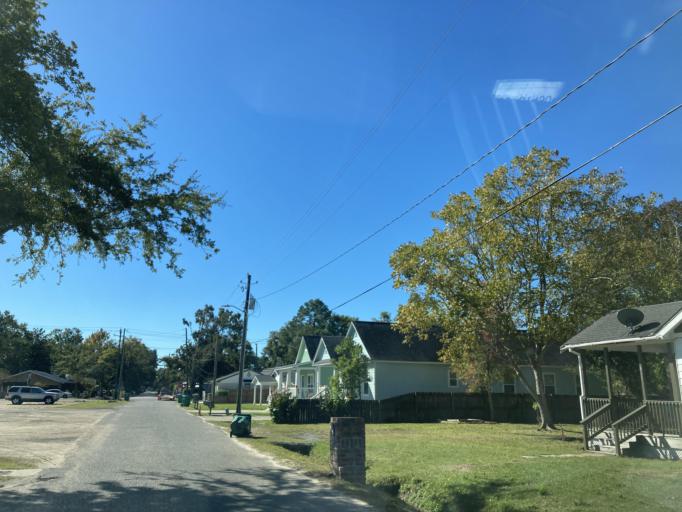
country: US
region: Mississippi
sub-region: Jackson County
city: Ocean Springs
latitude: 30.4146
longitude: -88.8224
